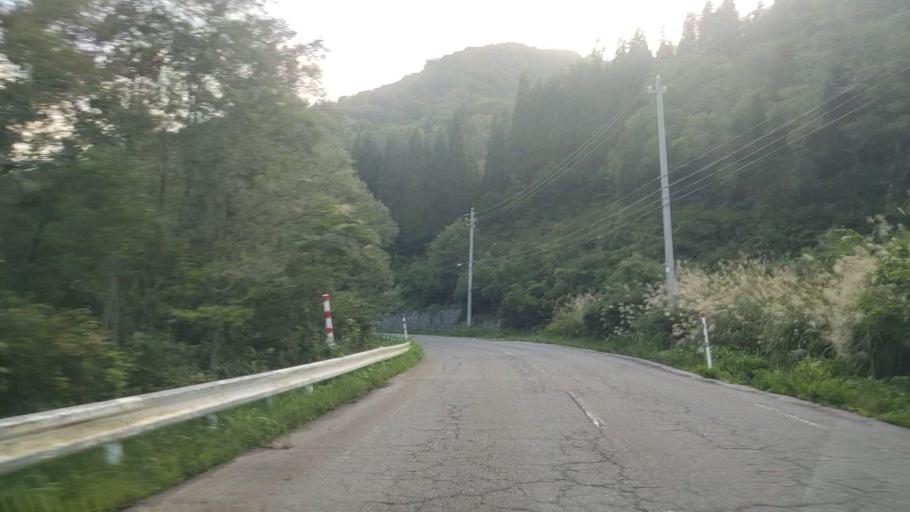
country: JP
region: Toyama
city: Yatsuomachi-higashikumisaka
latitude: 36.4833
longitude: 137.0487
